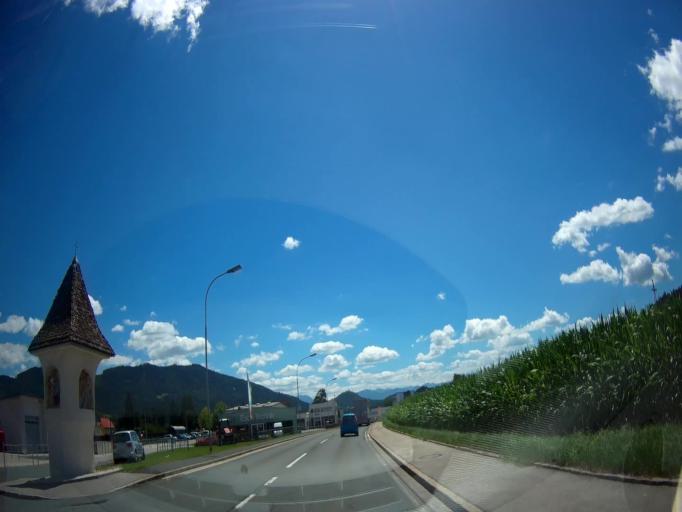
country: AT
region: Carinthia
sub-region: Politischer Bezirk Sankt Veit an der Glan
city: Sankt Veit an der Glan
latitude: 46.7528
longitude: 14.3800
